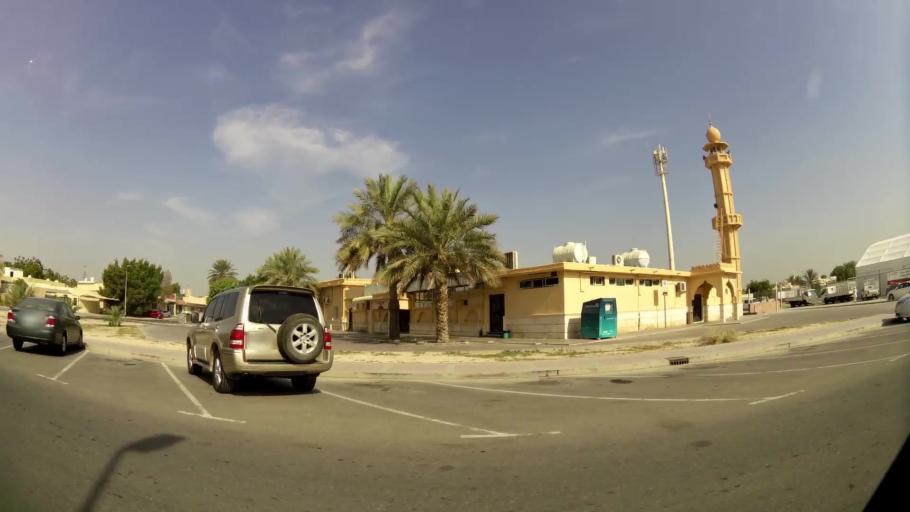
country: AE
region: Ash Shariqah
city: Sharjah
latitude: 25.2238
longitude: 55.3829
